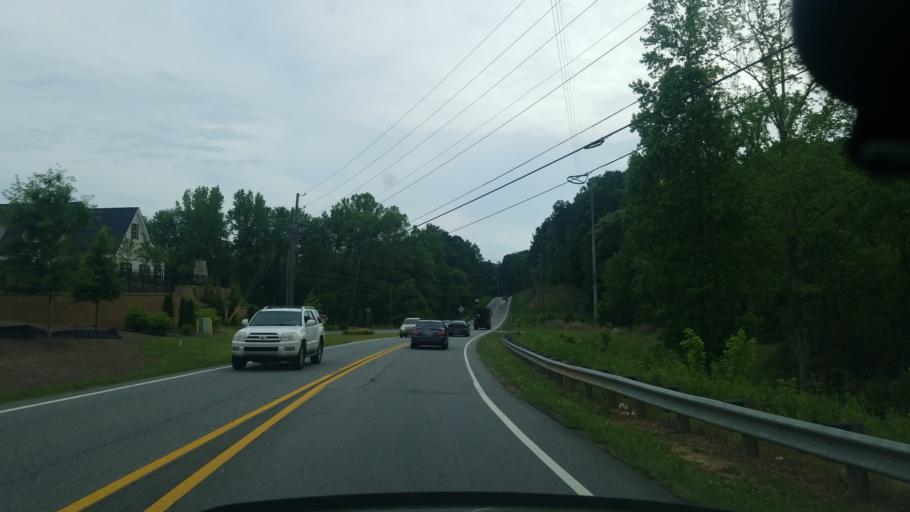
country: US
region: Georgia
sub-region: Gwinnett County
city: Suwanee
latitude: 34.0725
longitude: -84.1294
